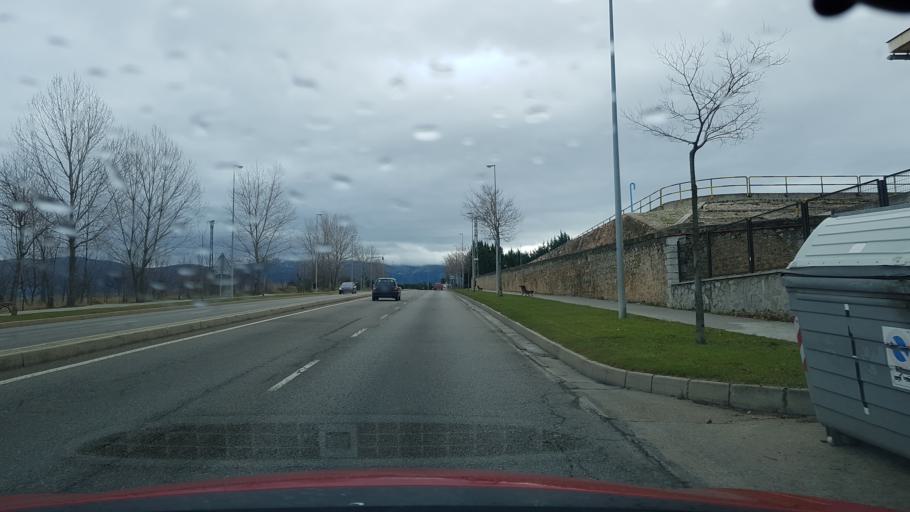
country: ES
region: Castille and Leon
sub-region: Provincia de Segovia
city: Segovia
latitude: 40.9383
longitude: -4.1018
